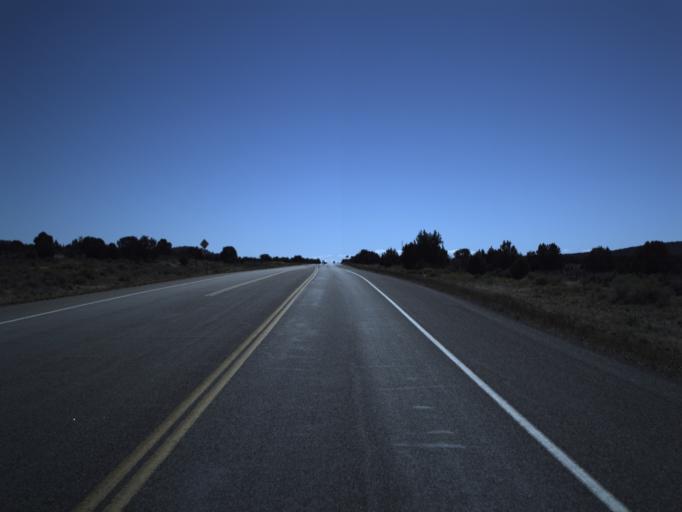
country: US
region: Utah
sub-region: Washington County
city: Ivins
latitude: 37.2996
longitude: -113.6665
